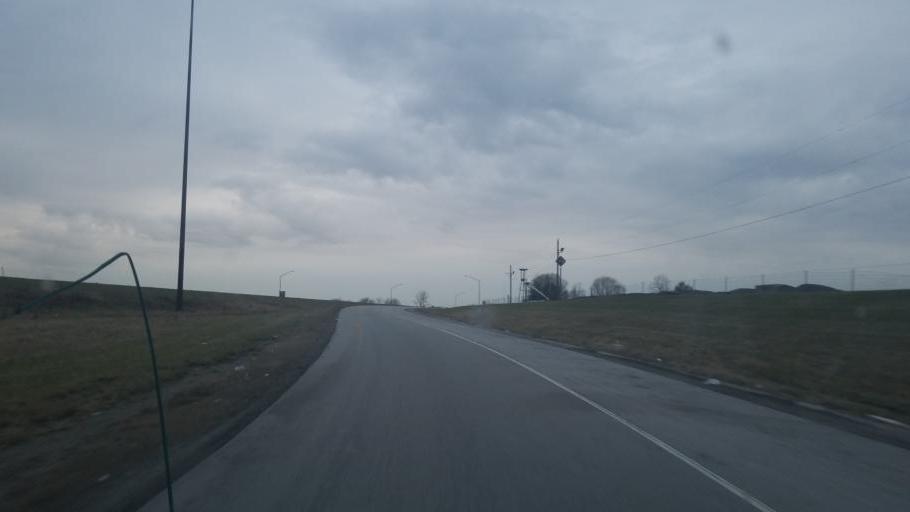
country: US
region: Indiana
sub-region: Clay County
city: Brazil
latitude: 39.4502
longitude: -87.1274
